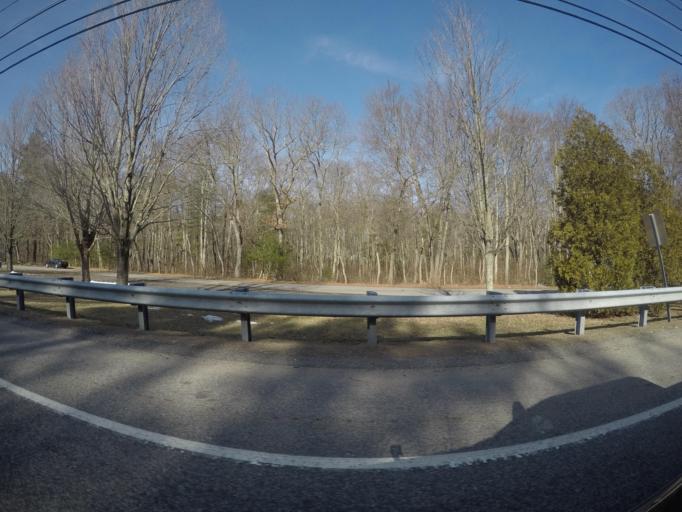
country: US
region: Massachusetts
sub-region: Bristol County
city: Easton
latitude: 42.0282
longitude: -71.1171
